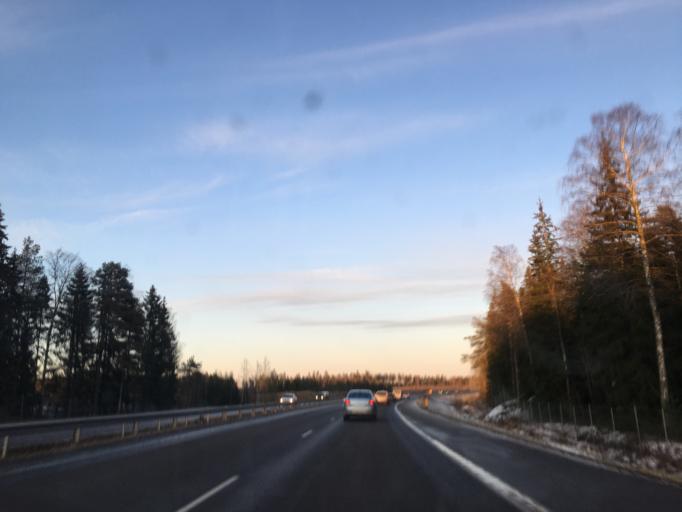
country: FI
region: Varsinais-Suomi
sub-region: Turku
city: Vahto
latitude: 60.5349
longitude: 22.3111
